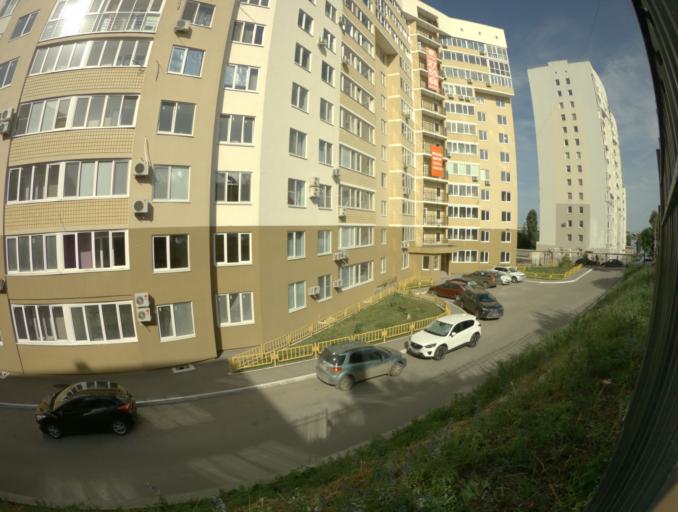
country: RU
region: Saratov
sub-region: Saratovskiy Rayon
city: Saratov
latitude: 51.5291
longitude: 46.0580
